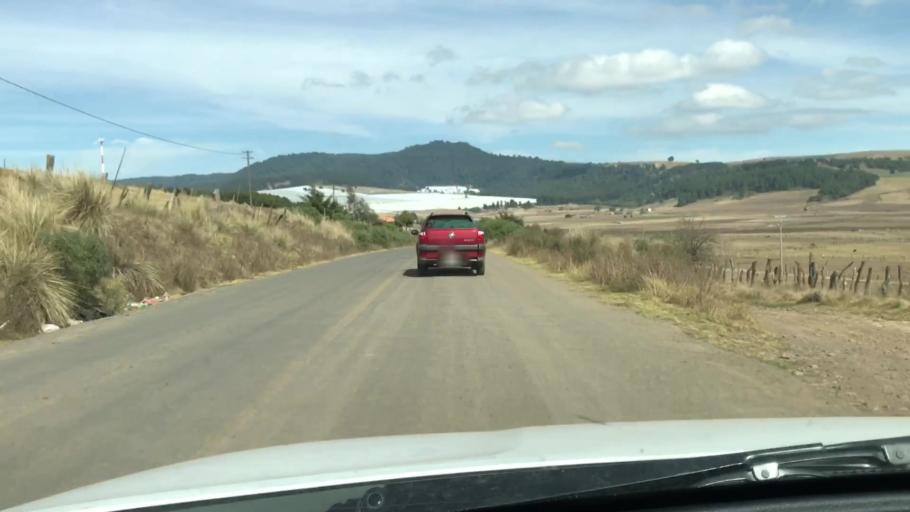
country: MX
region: Jalisco
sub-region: Amacueca
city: Tepec
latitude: 20.0168
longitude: -103.6928
